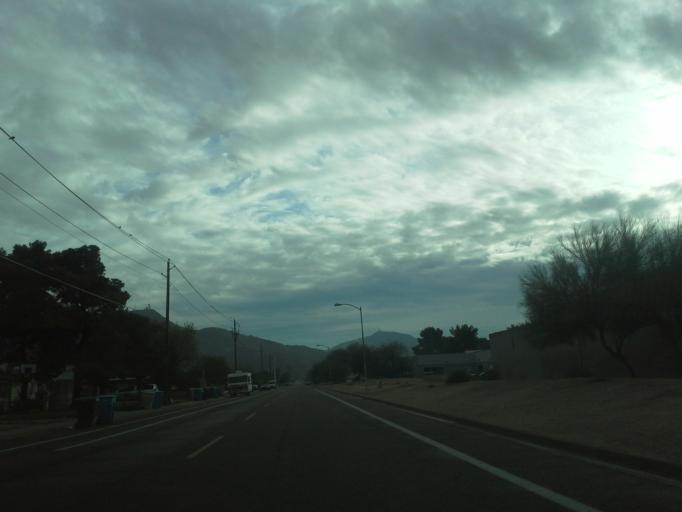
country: US
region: Arizona
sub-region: Maricopa County
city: Glendale
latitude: 33.5892
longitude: -112.1111
